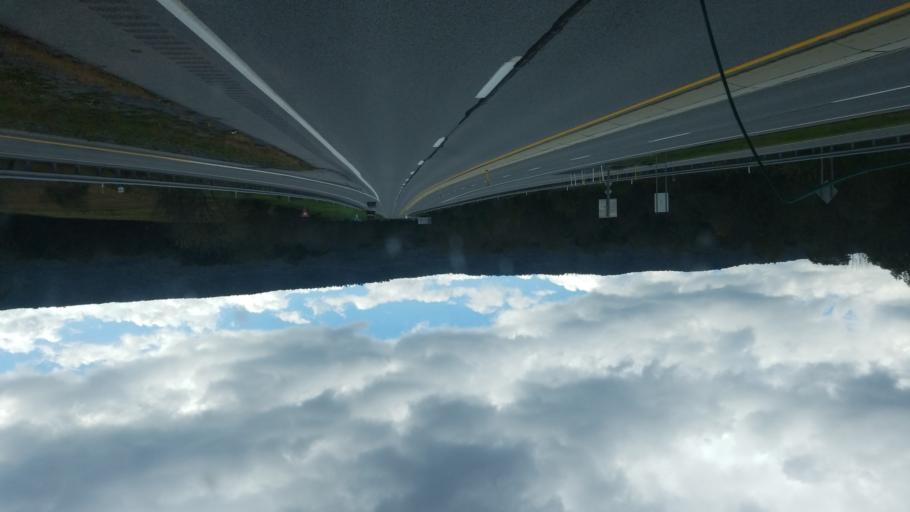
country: US
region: Pennsylvania
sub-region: Fulton County
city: McConnellsburg
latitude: 39.9433
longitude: -77.9912
